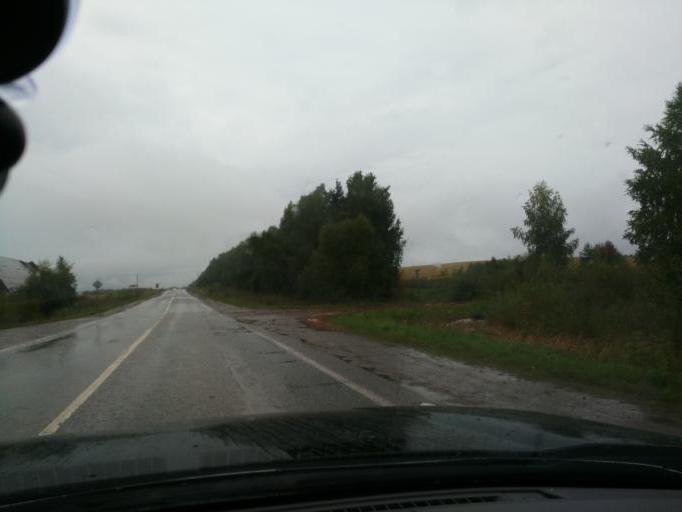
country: RU
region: Perm
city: Osa
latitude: 57.3749
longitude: 55.6098
